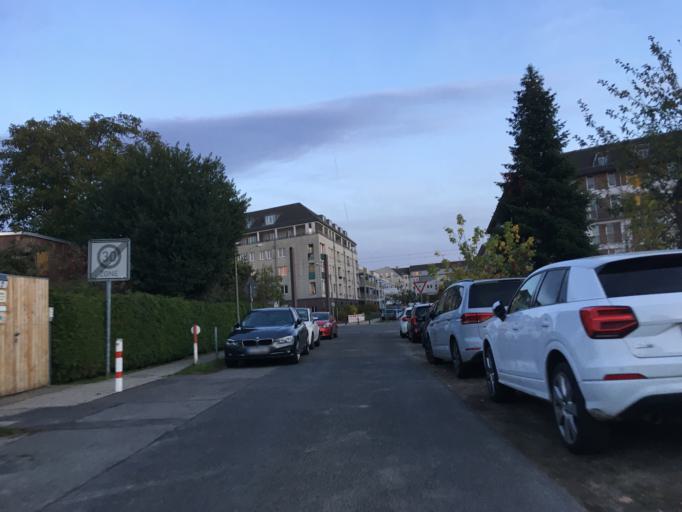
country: DE
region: Berlin
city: Buchholz
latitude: 52.6058
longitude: 13.4165
